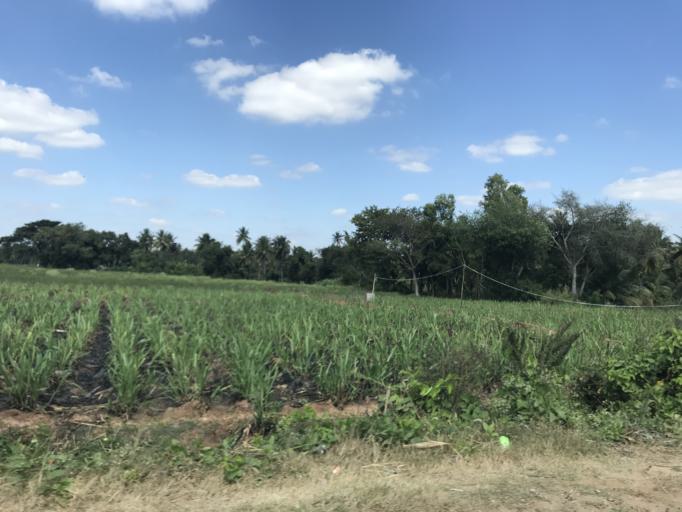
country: IN
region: Karnataka
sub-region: Mandya
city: Krishnarajpet
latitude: 12.5924
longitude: 76.3560
